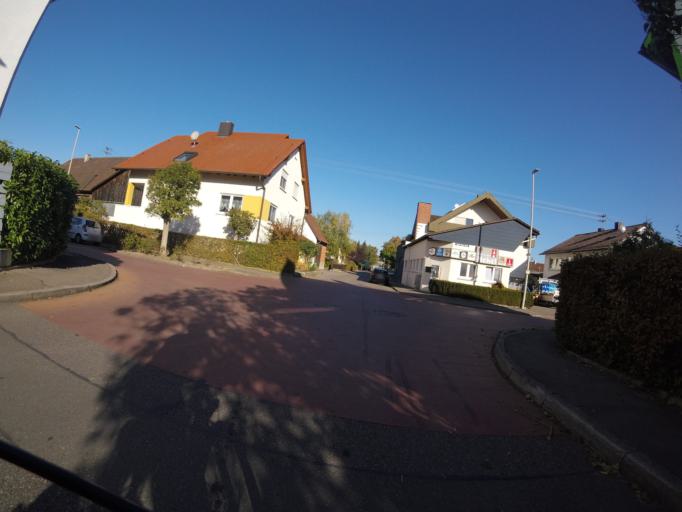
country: DE
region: Baden-Wuerttemberg
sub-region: Regierungsbezirk Stuttgart
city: Murr
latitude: 48.9635
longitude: 9.2574
